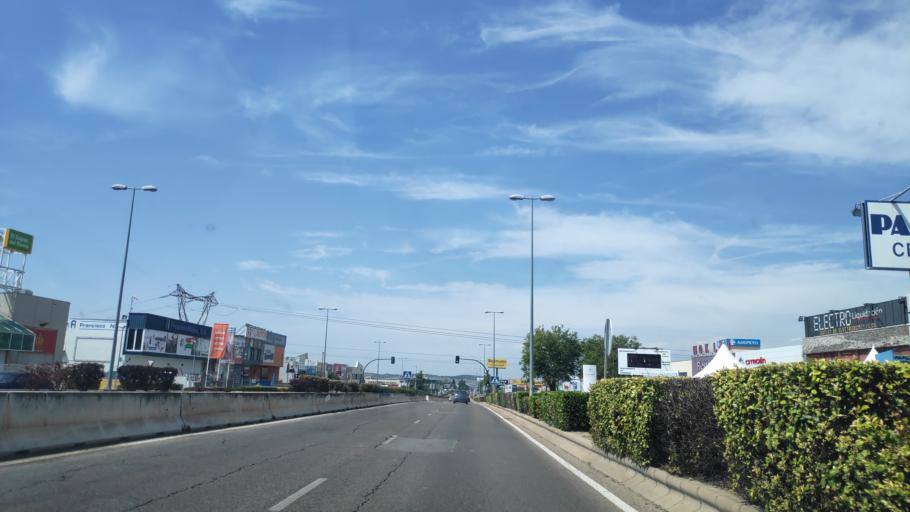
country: ES
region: Madrid
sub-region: Provincia de Madrid
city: Arganda
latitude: 40.3049
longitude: -3.4565
